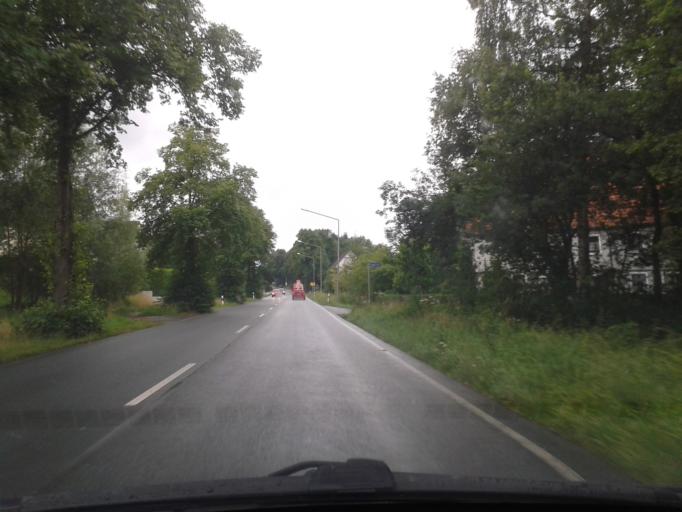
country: DE
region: North Rhine-Westphalia
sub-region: Regierungsbezirk Detmold
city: Detmold
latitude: 51.9652
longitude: 8.8910
